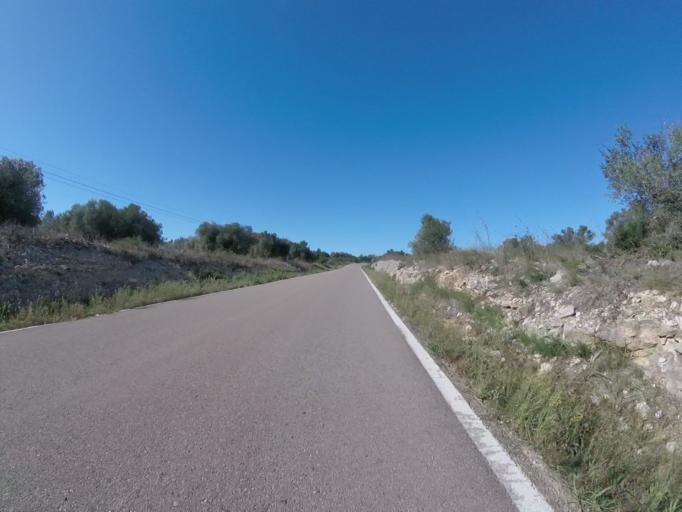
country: ES
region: Valencia
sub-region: Provincia de Castello
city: Chert/Xert
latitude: 40.4572
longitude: 0.1492
